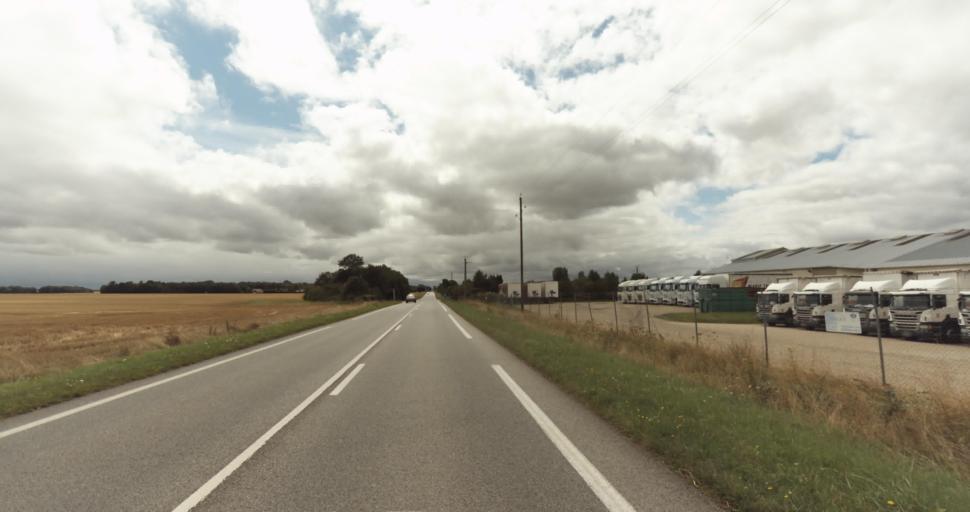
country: FR
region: Haute-Normandie
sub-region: Departement de l'Eure
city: Evreux
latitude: 48.9812
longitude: 1.1578
